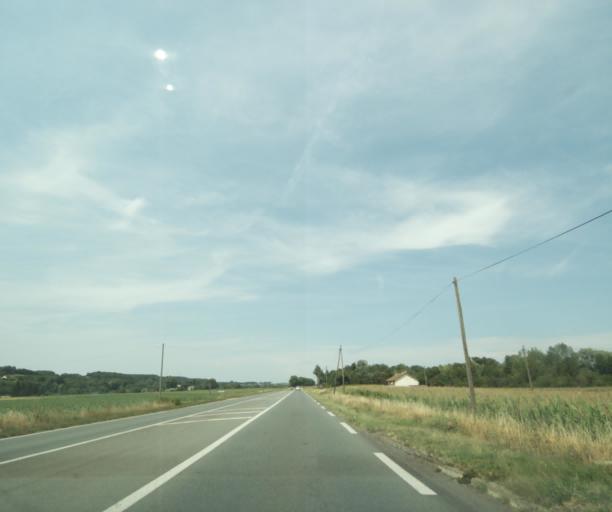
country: FR
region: Poitou-Charentes
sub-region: Departement de la Vienne
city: Antran
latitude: 46.8874
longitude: 0.5685
